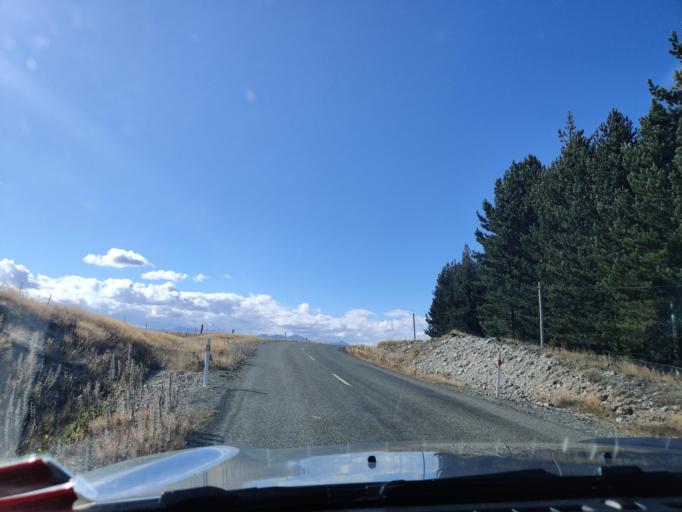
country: NZ
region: Canterbury
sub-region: Timaru District
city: Pleasant Point
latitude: -43.9987
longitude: 170.4507
